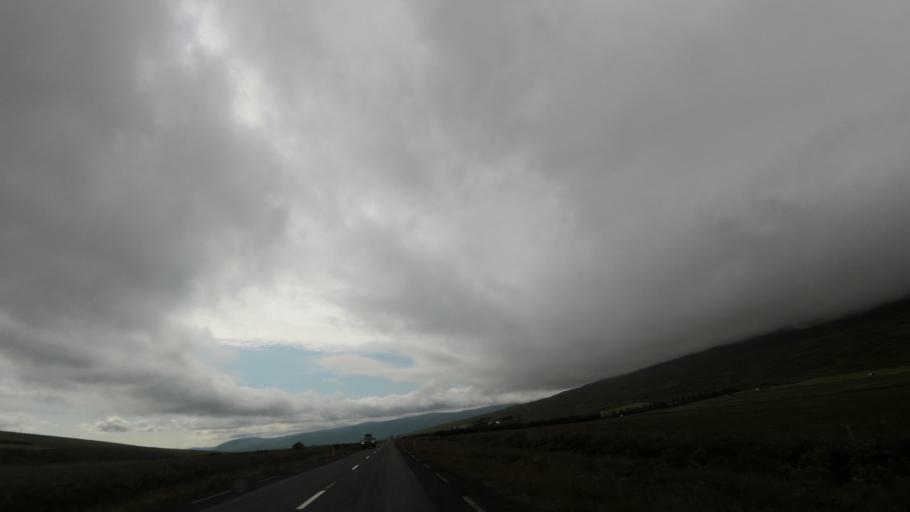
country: IS
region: Northeast
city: Laugar
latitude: 65.7567
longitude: -17.5843
